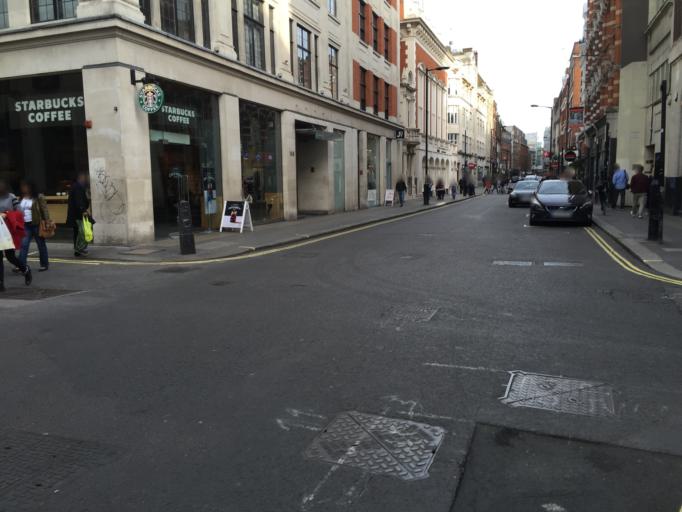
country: GB
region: England
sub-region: Greater London
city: London
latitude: 51.5154
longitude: -0.1354
